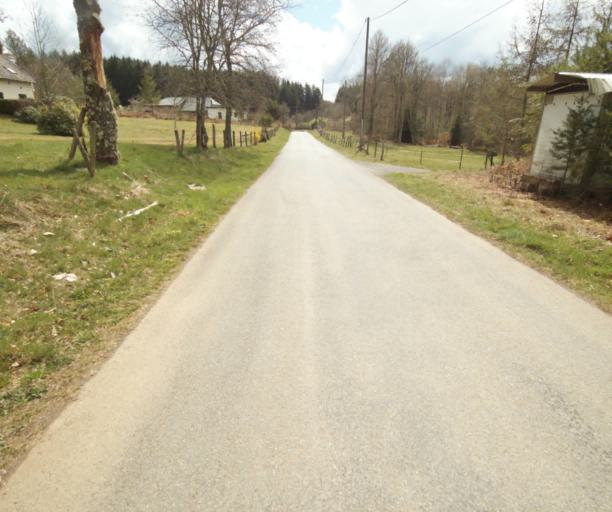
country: FR
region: Limousin
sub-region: Departement de la Correze
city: Correze
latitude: 45.3270
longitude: 1.9168
